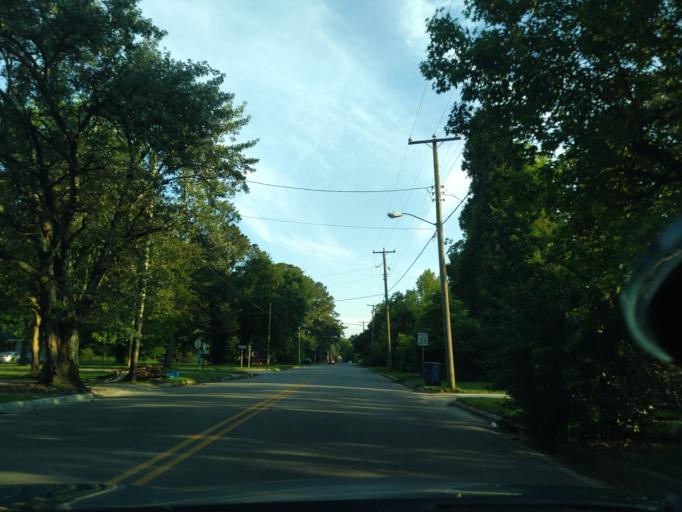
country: US
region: North Carolina
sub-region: Washington County
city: Plymouth
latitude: 35.8603
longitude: -76.7539
